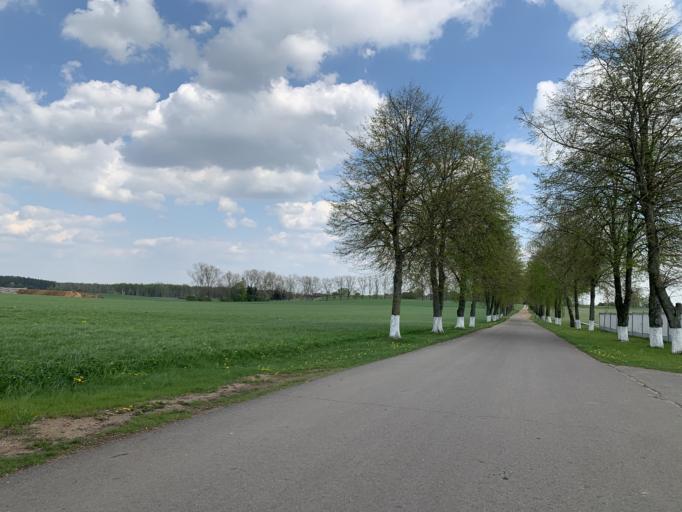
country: BY
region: Minsk
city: Nyasvizh
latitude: 53.2463
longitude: 26.6880
